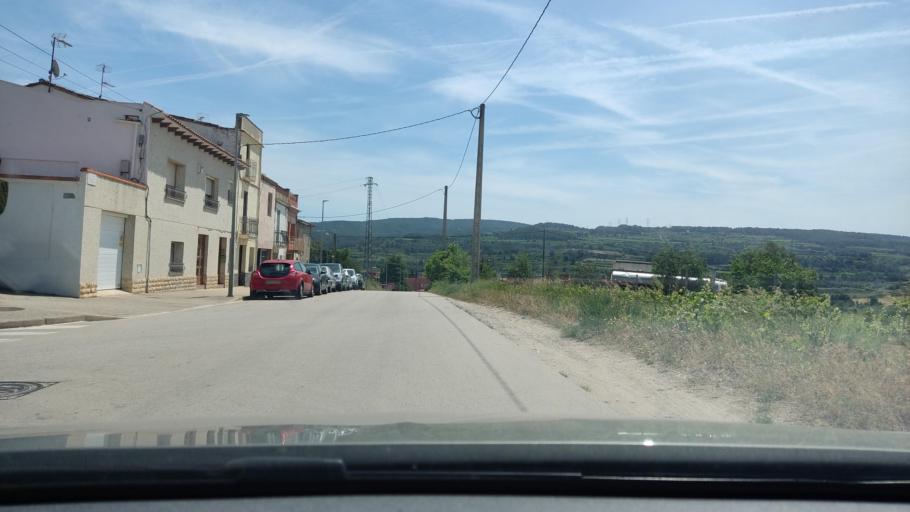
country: ES
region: Catalonia
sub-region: Provincia de Barcelona
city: Sant Sadurni d'Anoia
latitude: 41.4231
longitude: 1.7766
